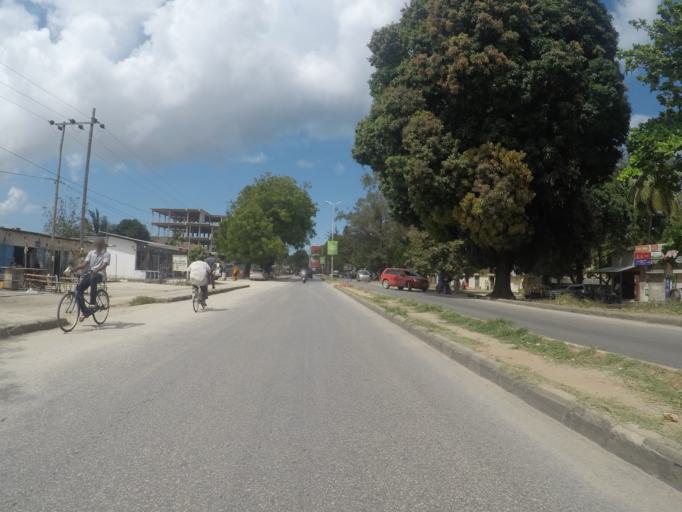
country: TZ
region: Zanzibar Urban/West
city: Zanzibar
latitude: -6.1965
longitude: 39.2157
